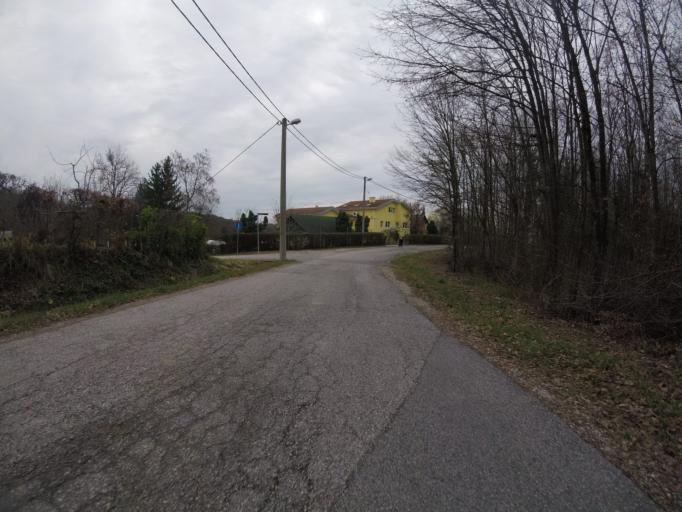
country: HR
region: Grad Zagreb
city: Strmec
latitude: 45.6323
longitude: 15.9362
